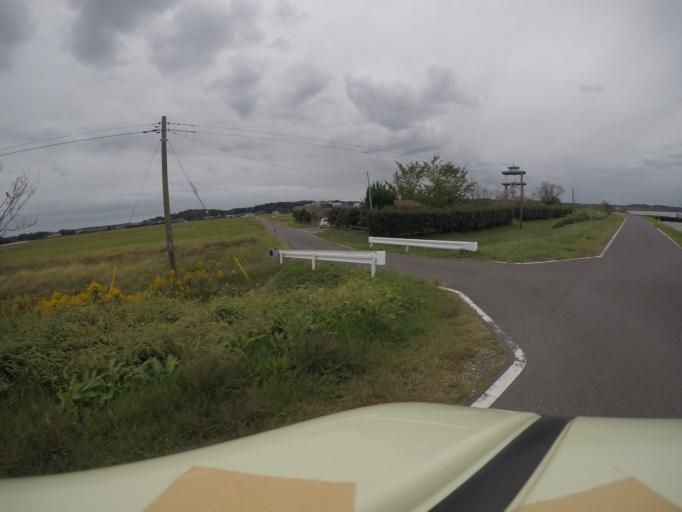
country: JP
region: Ibaraki
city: Inashiki
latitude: 36.0302
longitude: 140.3097
